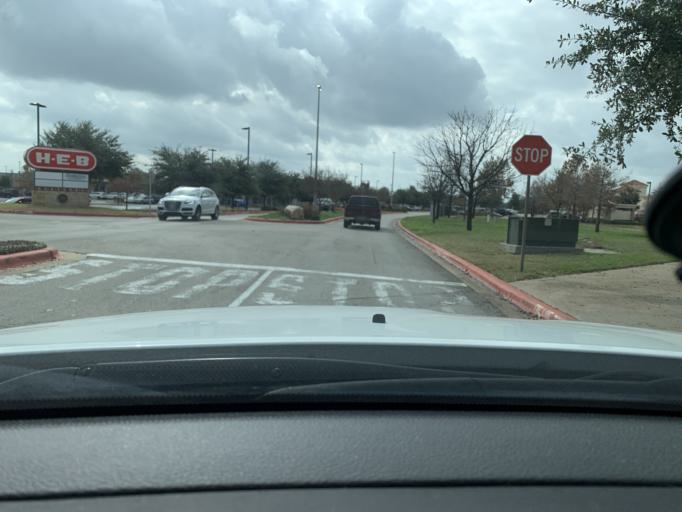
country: US
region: Texas
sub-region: Williamson County
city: Round Rock
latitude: 30.5629
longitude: -97.6900
